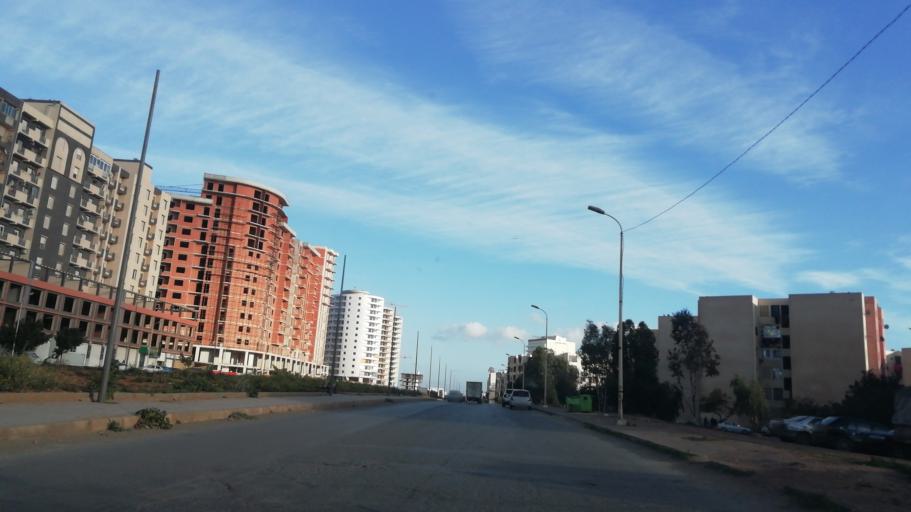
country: DZ
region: Oran
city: Bir el Djir
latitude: 35.7095
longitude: -0.5659
